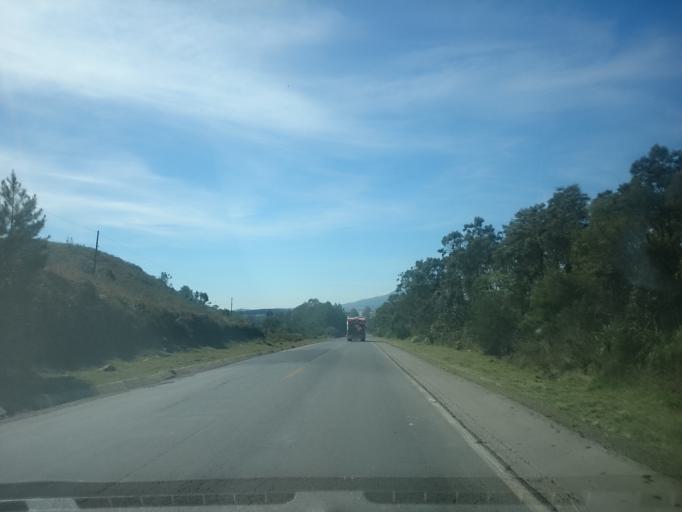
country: BR
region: Santa Catarina
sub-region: Lages
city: Lages
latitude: -27.7759
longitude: -50.2153
